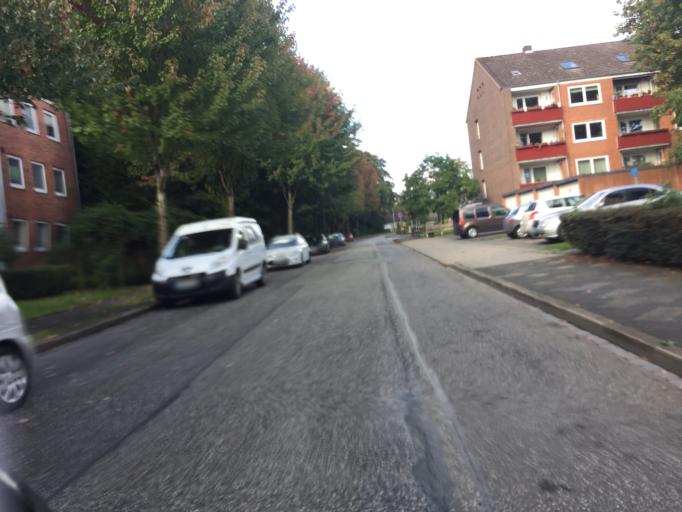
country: DE
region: Schleswig-Holstein
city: Heiligenstedten
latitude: 53.9386
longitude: 9.4923
